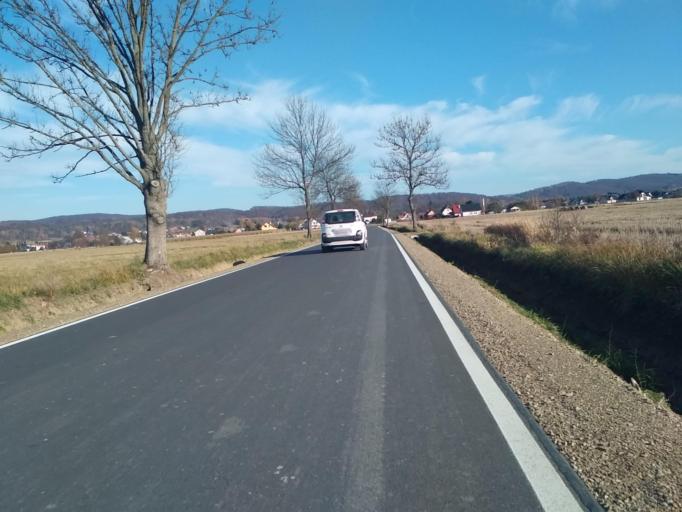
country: PL
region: Subcarpathian Voivodeship
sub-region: Powiat brzozowski
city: Humniska
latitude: 49.6703
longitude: 22.0377
